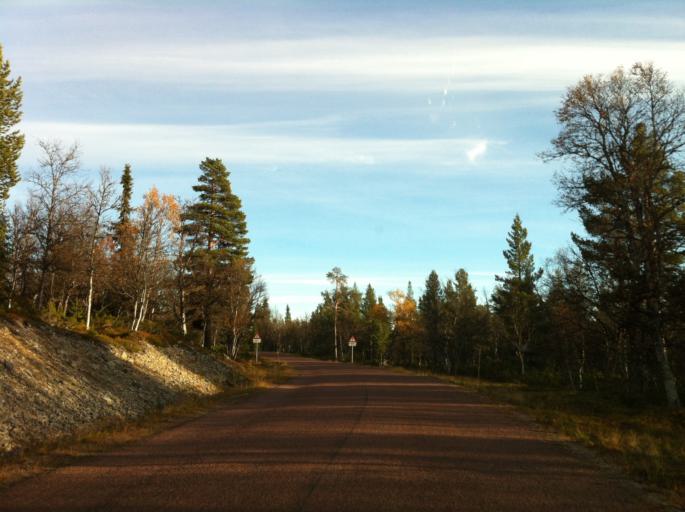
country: NO
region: Hedmark
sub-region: Engerdal
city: Engerdal
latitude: 62.0768
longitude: 12.1710
